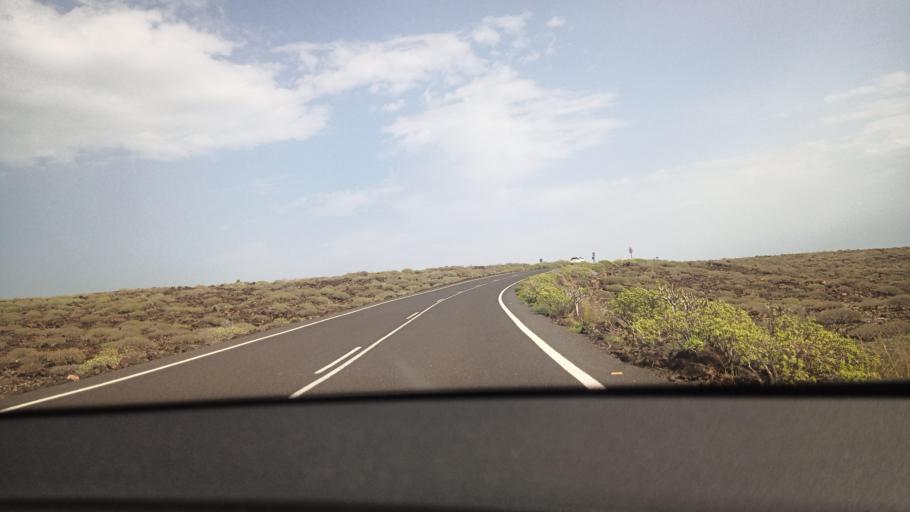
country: ES
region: Canary Islands
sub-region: Provincia de Las Palmas
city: Haria
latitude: 29.1554
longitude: -13.4374
